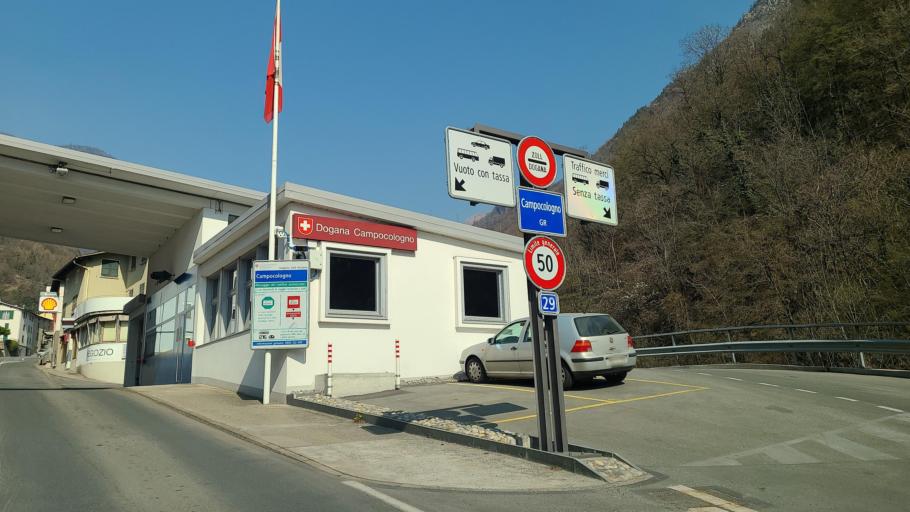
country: IT
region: Lombardy
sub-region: Provincia di Sondrio
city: Tirano
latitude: 46.2303
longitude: 10.1456
